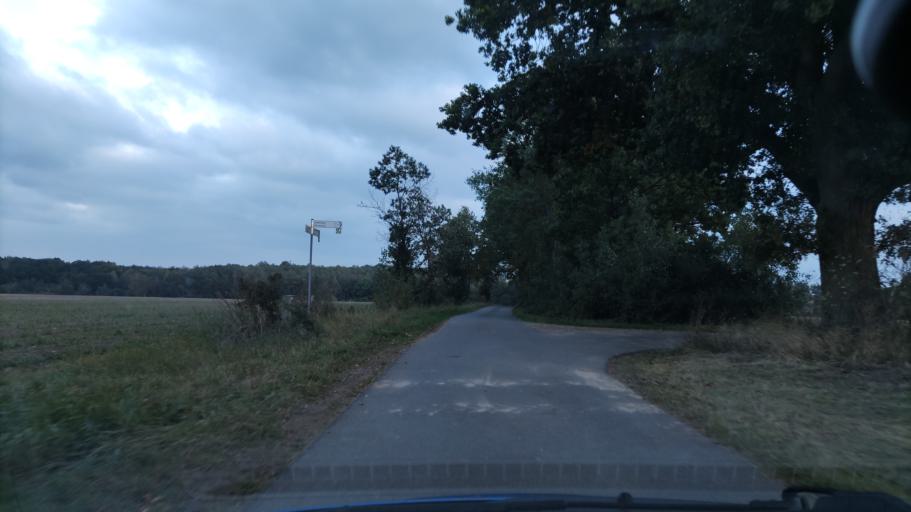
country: DE
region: Lower Saxony
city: Tosterglope
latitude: 53.2216
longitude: 10.8295
